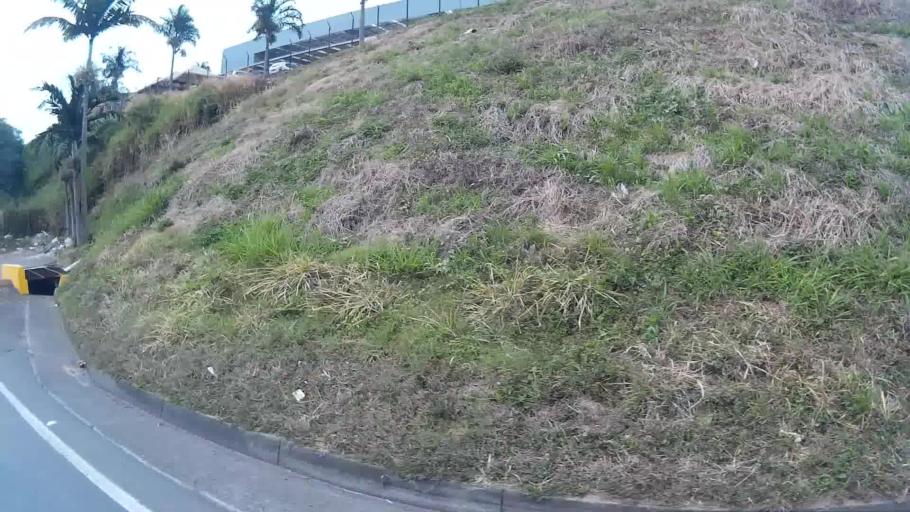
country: CO
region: Risaralda
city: Pereira
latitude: 4.8141
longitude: -75.7660
